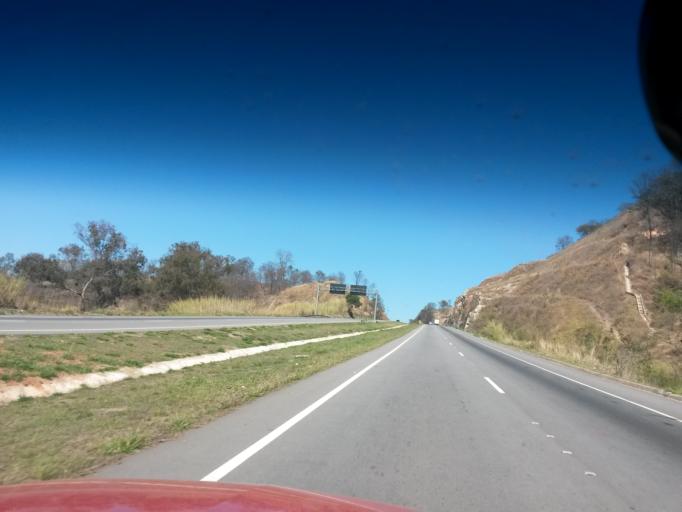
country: BR
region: Minas Gerais
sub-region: Para De Minas
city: Para de Minas
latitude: -19.8920
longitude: -44.6515
